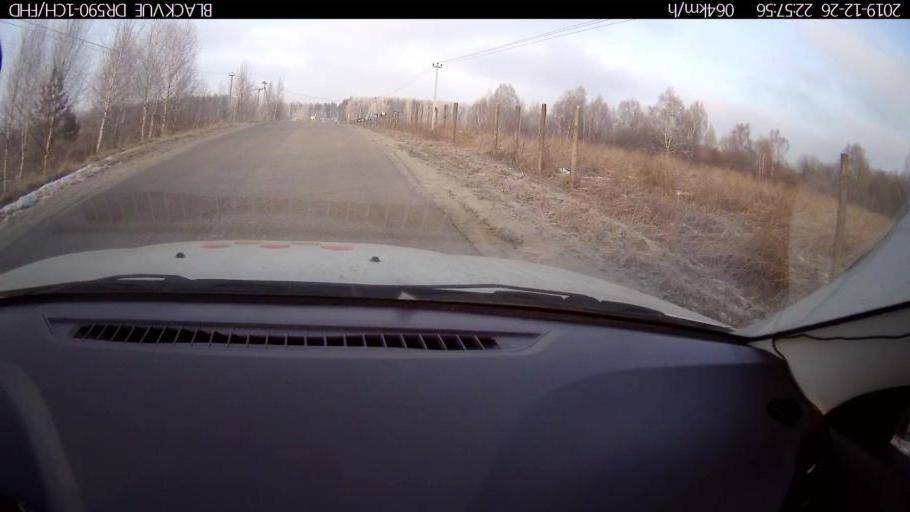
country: RU
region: Nizjnij Novgorod
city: Burevestnik
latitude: 56.1545
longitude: 43.7120
